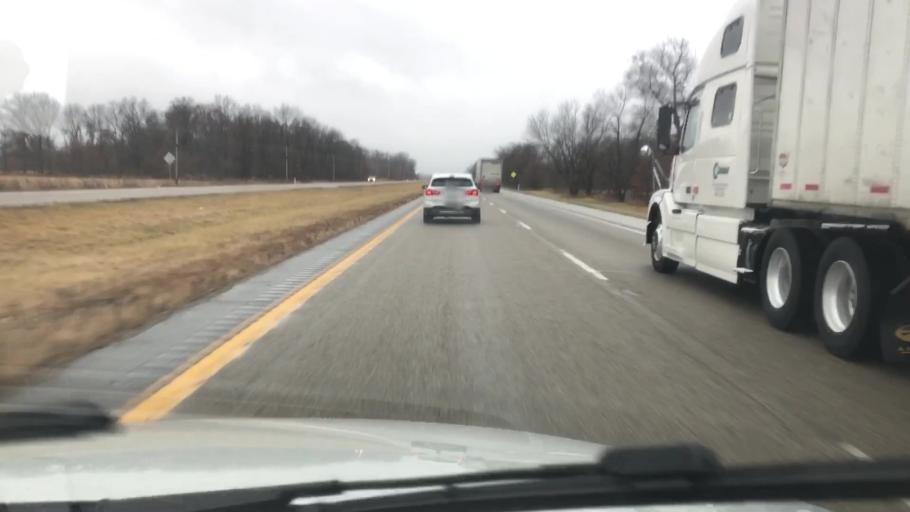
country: US
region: Indiana
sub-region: LaPorte County
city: Wanatah
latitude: 41.4338
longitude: -86.8357
